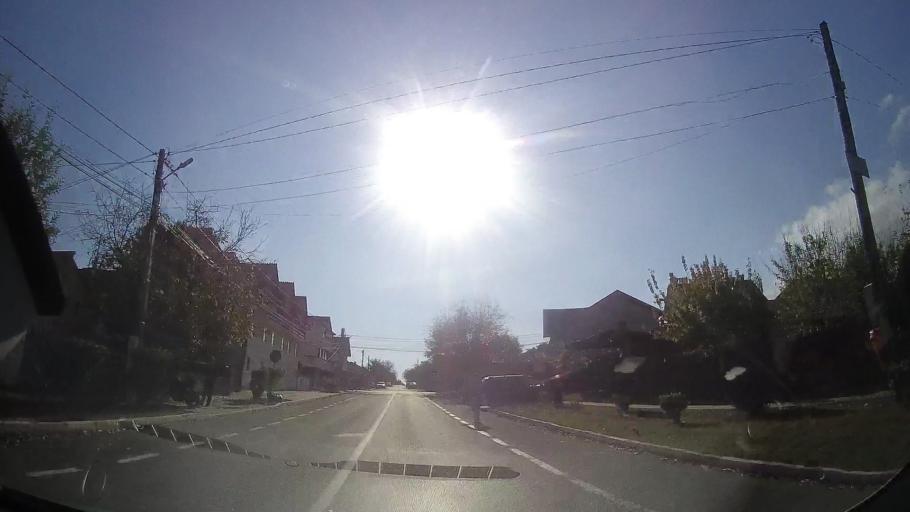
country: RO
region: Constanta
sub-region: Comuna Costinesti
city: Schitu
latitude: 43.9417
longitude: 28.6292
